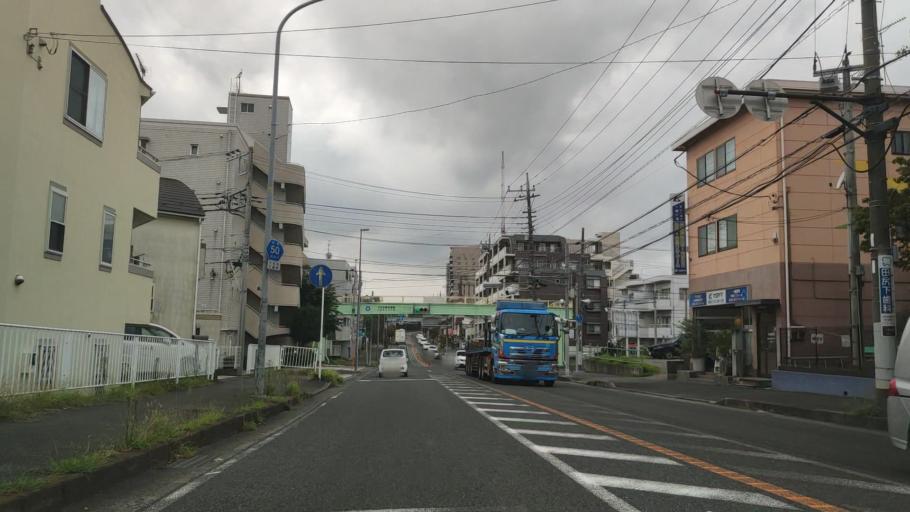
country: JP
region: Kanagawa
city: Minami-rinkan
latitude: 35.5037
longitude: 139.4621
